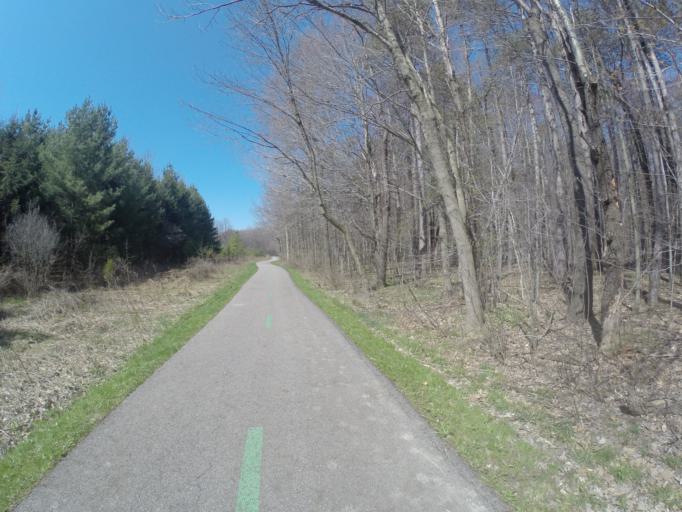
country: US
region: Ohio
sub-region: Cuyahoga County
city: Mayfield
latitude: 41.5707
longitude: -81.4336
